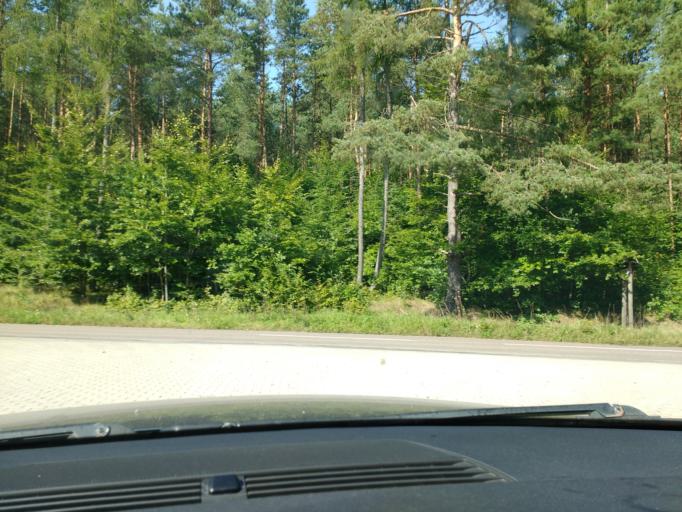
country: PL
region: Pomeranian Voivodeship
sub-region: Powiat wejherowski
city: Bojano
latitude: 54.5198
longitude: 18.4149
